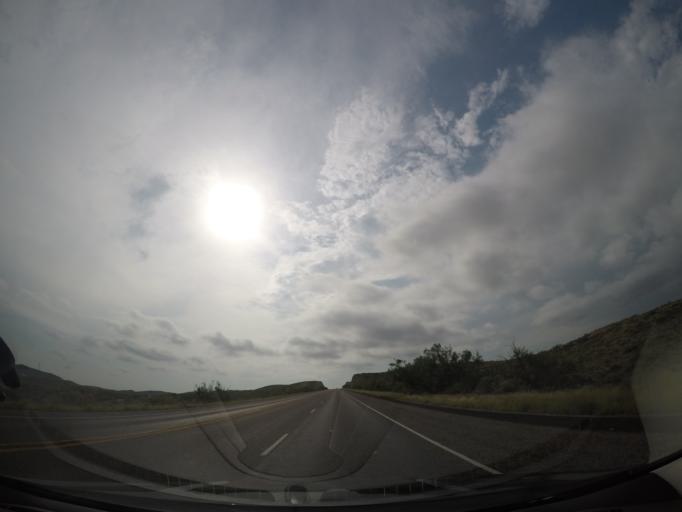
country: US
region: Texas
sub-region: Val Verde County
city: Cienegas Terrace
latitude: 29.8106
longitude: -101.5144
